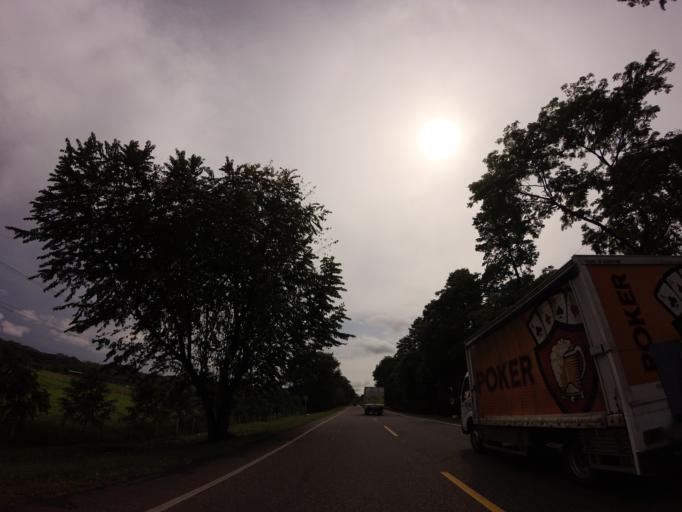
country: CO
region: Caldas
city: La Dorada
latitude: 5.4031
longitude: -74.6945
